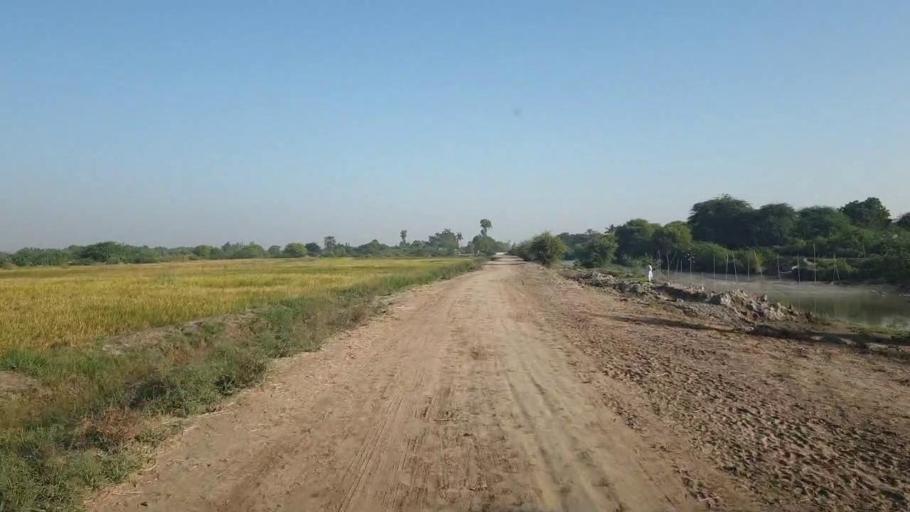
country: PK
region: Sindh
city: Badin
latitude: 24.6856
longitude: 68.8154
